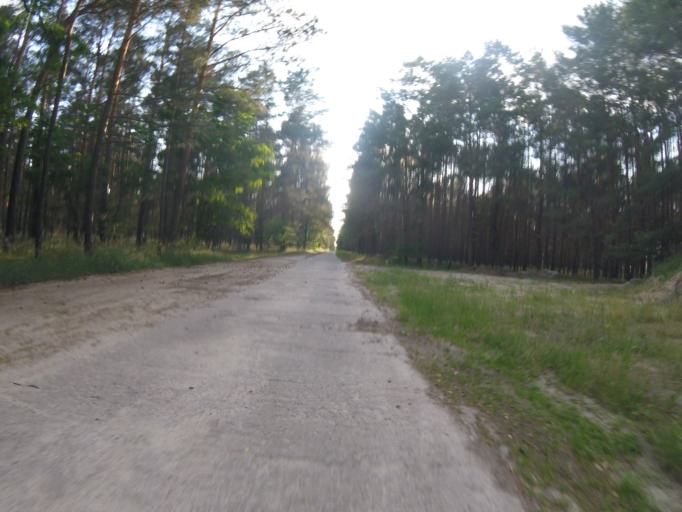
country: DE
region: Brandenburg
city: Schwerin
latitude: 52.1980
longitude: 13.5985
